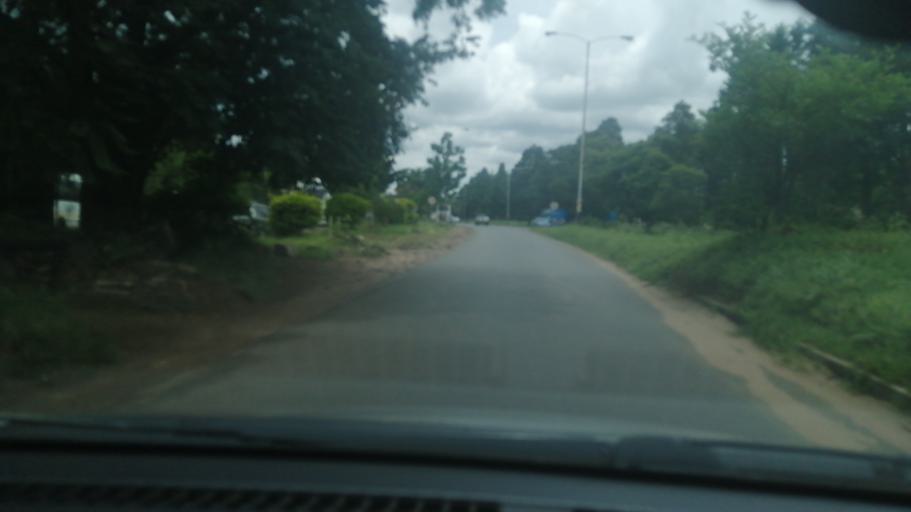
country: ZW
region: Harare
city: Harare
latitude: -17.8304
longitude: 31.0717
